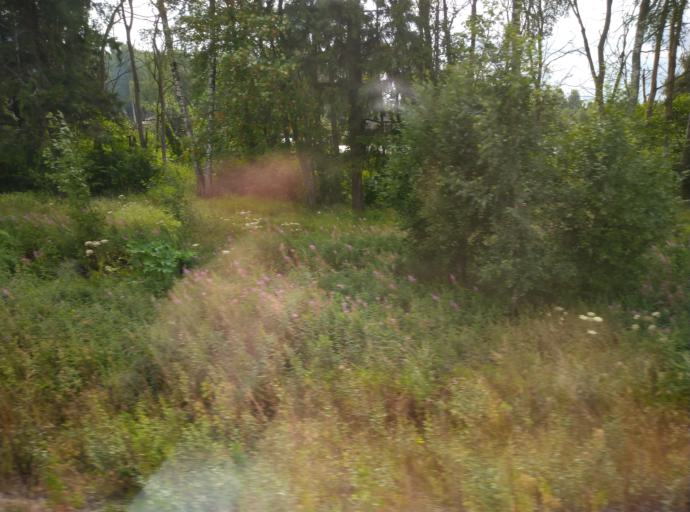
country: RU
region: Jaroslavl
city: Tunoshna
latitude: 57.4936
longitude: 40.1135
